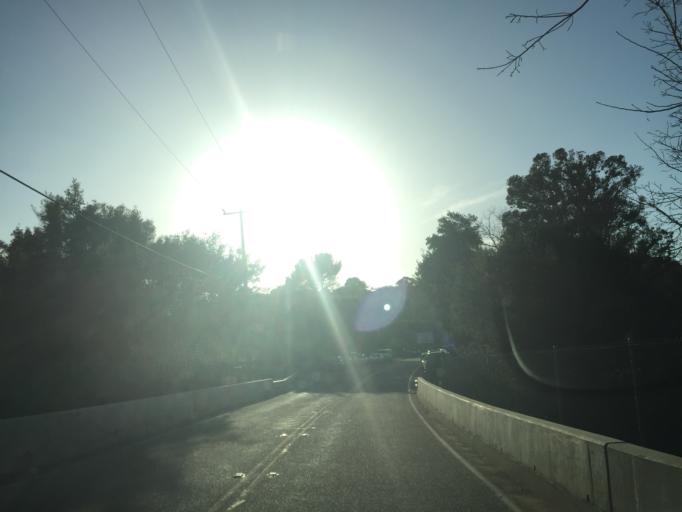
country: US
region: California
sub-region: Los Angeles County
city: Agoura
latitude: 34.1035
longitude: -118.7127
